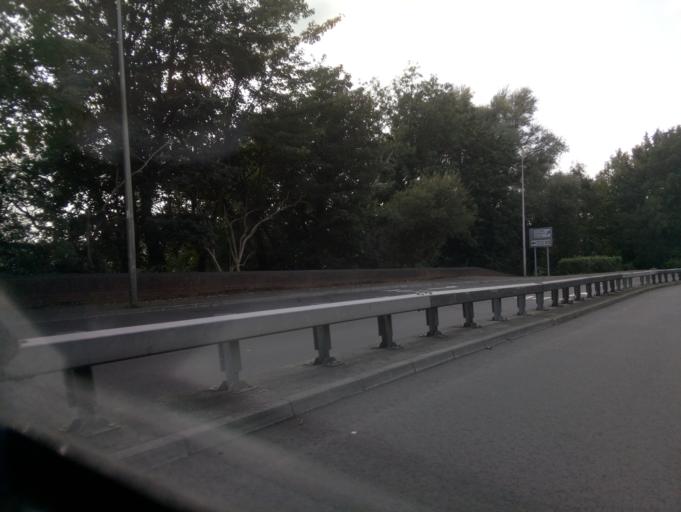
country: GB
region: Wales
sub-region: Caerphilly County Borough
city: Abertridwr
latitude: 51.5745
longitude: -3.2910
